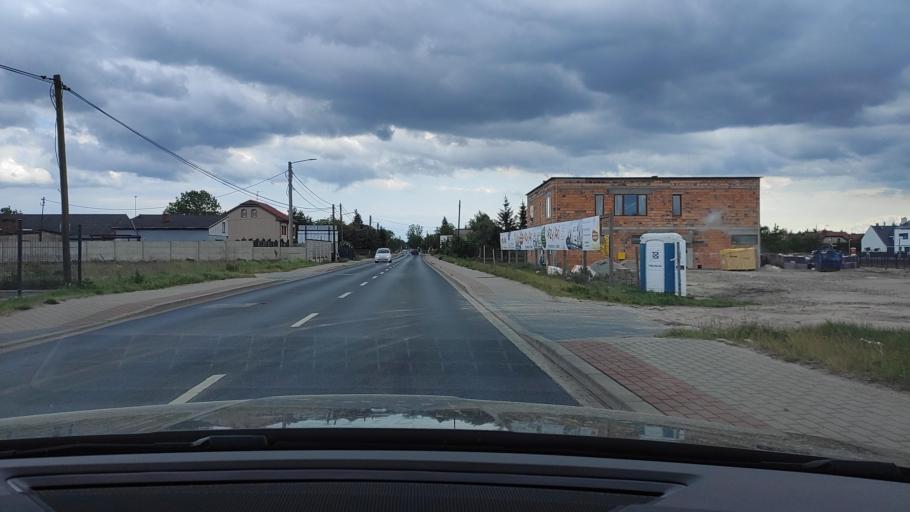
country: PL
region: Greater Poland Voivodeship
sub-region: Powiat poznanski
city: Swarzedz
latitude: 52.3941
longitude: 17.0767
